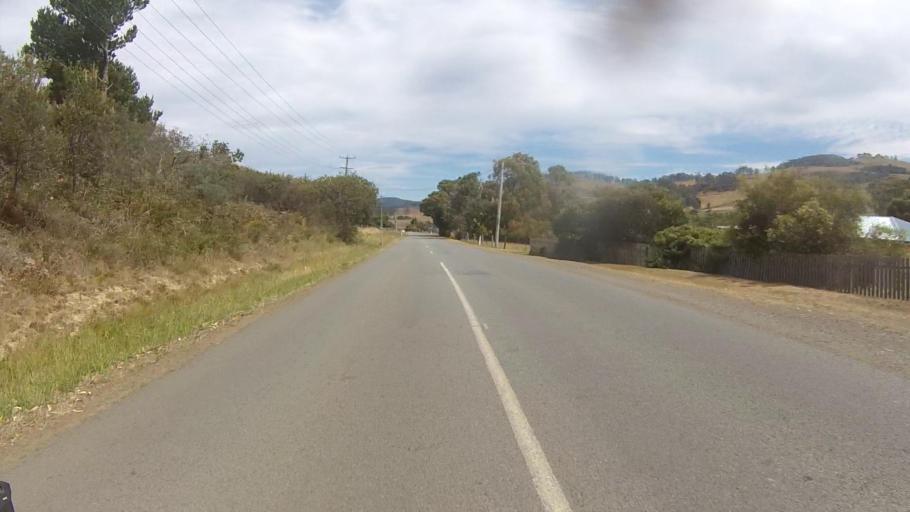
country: AU
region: Tasmania
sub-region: Sorell
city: Sorell
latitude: -42.8208
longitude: 147.8201
